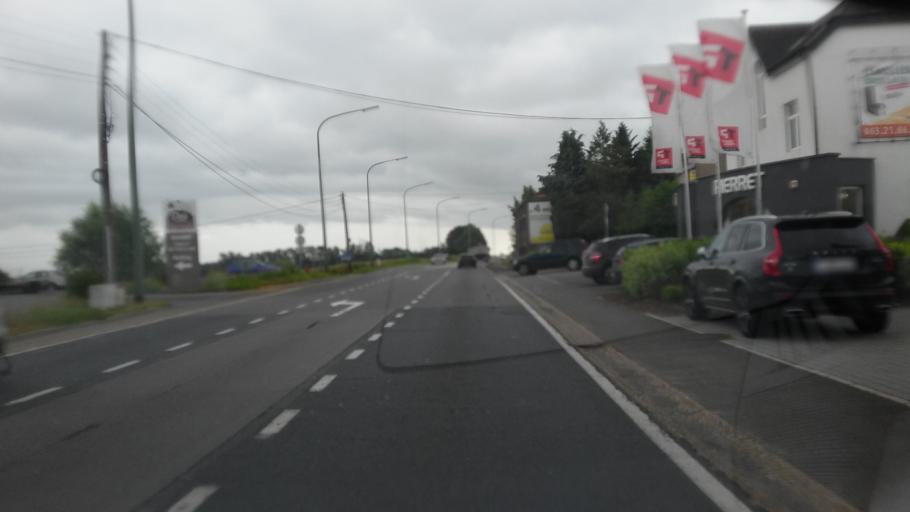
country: BE
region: Wallonia
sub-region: Province du Luxembourg
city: Arlon
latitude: 49.6683
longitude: 5.8241
